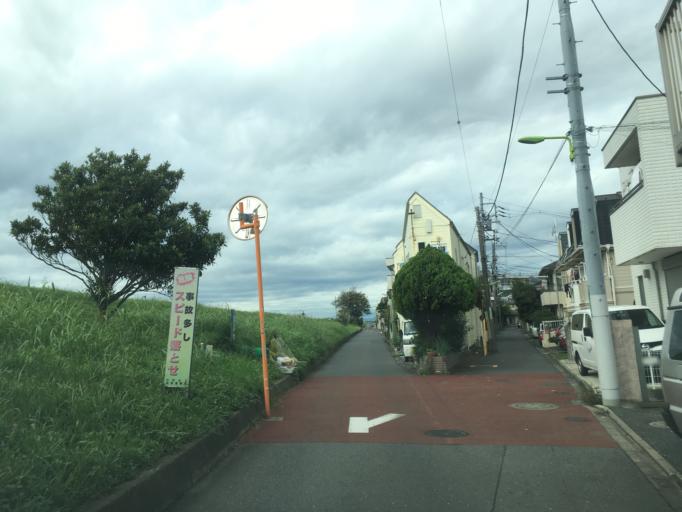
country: JP
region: Tokyo
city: Chofugaoka
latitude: 35.6171
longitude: 139.6100
